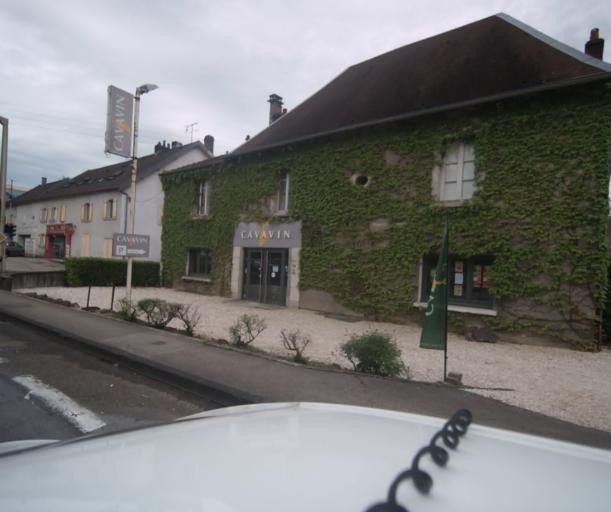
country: FR
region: Franche-Comte
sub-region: Departement du Doubs
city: Beure
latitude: 47.2293
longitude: 5.9900
